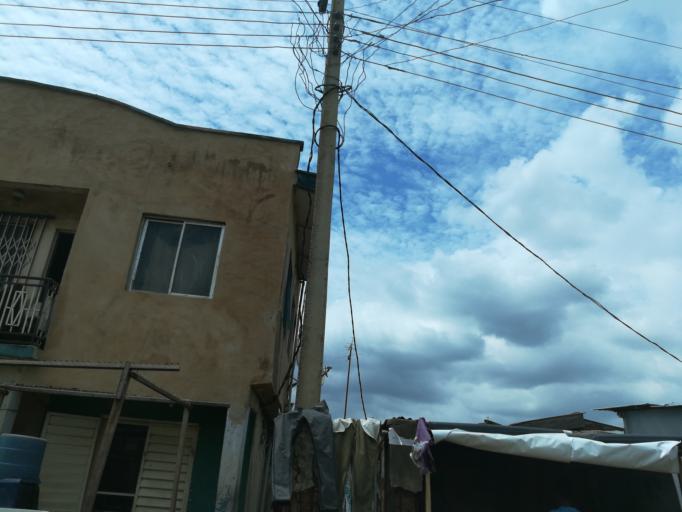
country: NG
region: Lagos
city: Oshodi
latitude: 6.5639
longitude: 3.3305
